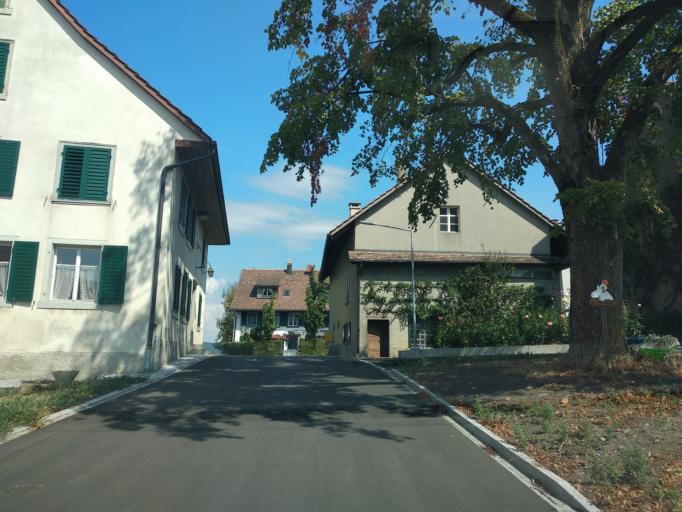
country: CH
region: Thurgau
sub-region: Frauenfeld District
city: Huttwilen
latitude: 47.5954
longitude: 8.8185
